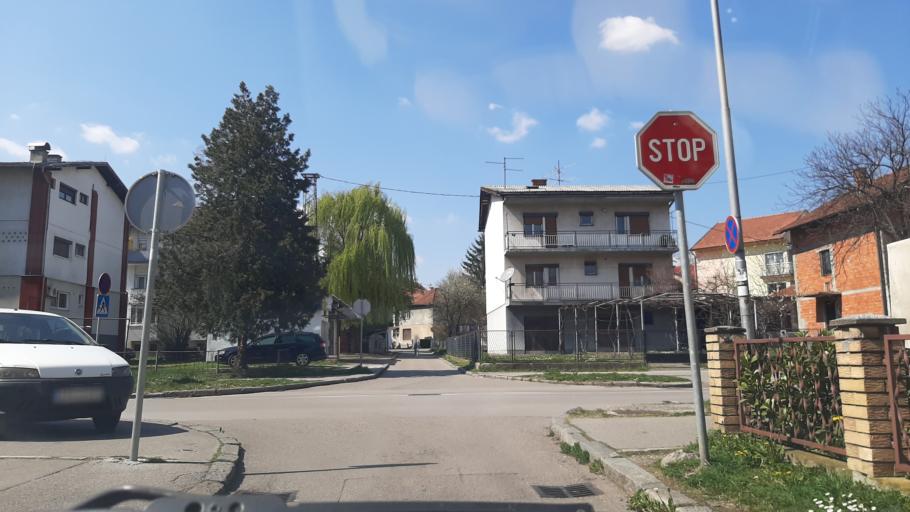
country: BA
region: Republika Srpska
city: Banja Luka
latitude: 44.7812
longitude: 17.1932
